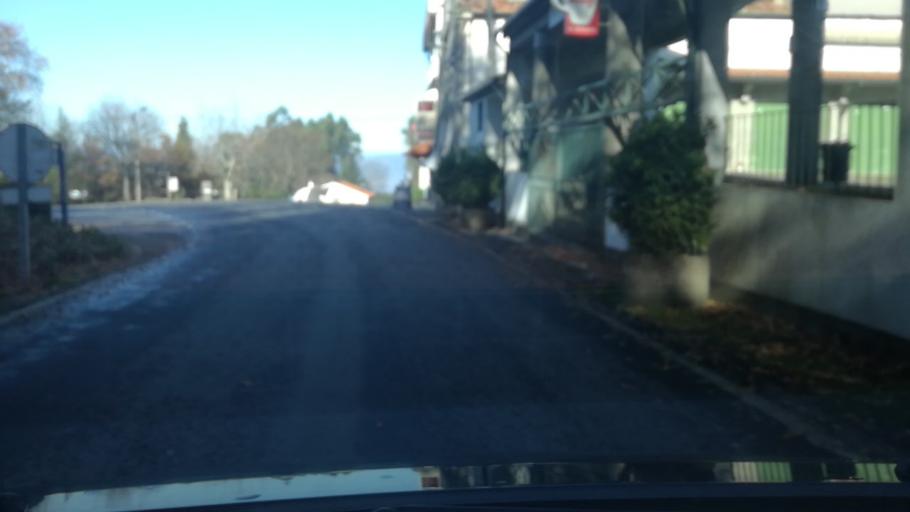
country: PT
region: Braga
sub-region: Braga
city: Braga
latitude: 41.5432
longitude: -8.3693
